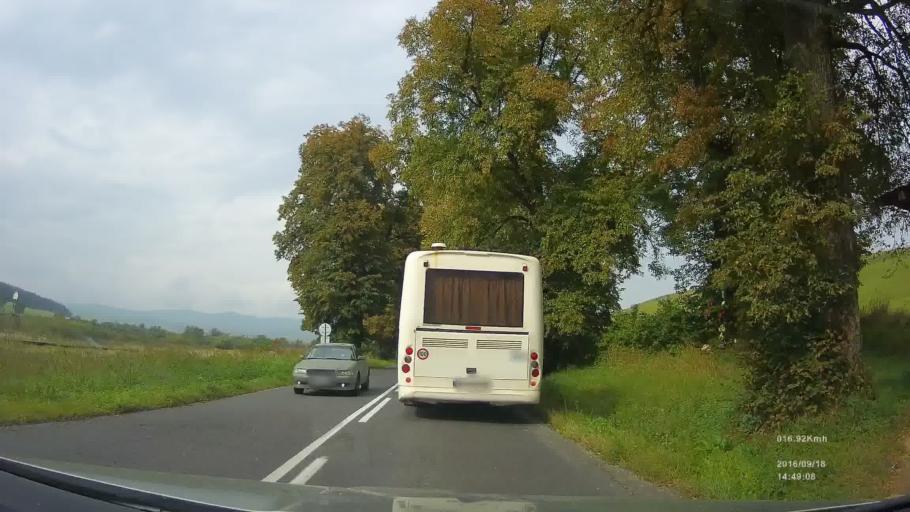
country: SK
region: Presovsky
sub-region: Okres Presov
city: Levoca
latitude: 48.9823
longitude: 20.5800
